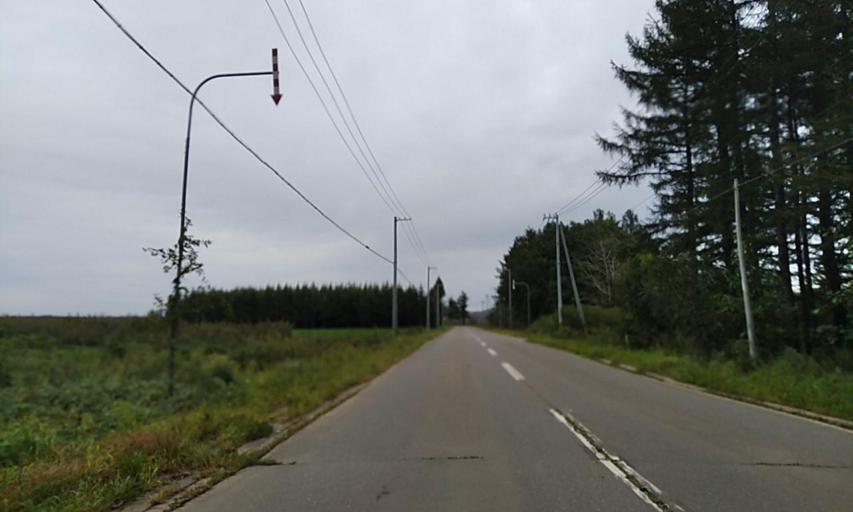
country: JP
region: Hokkaido
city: Obihiro
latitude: 42.6164
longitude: 143.2566
